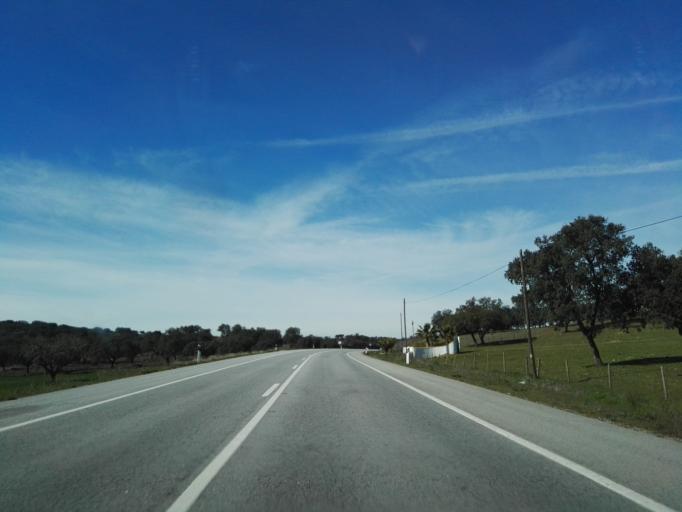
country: PT
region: Portalegre
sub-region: Portalegre
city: Urra
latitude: 39.1903
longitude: -7.3563
